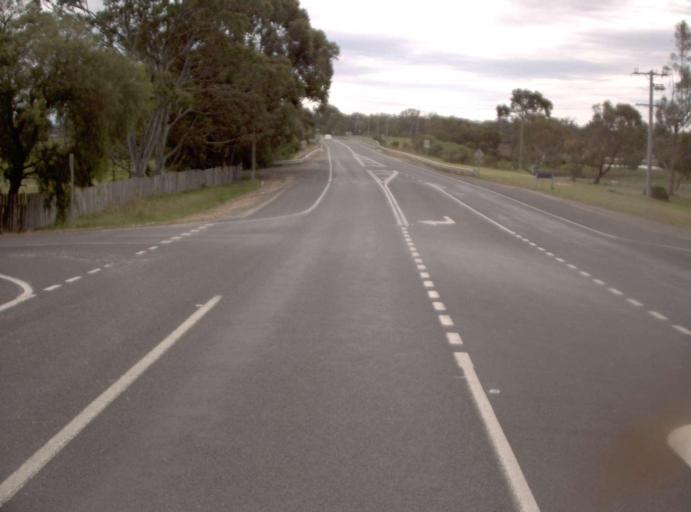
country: AU
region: Victoria
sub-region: Wellington
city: Sale
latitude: -38.1568
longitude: 147.0838
